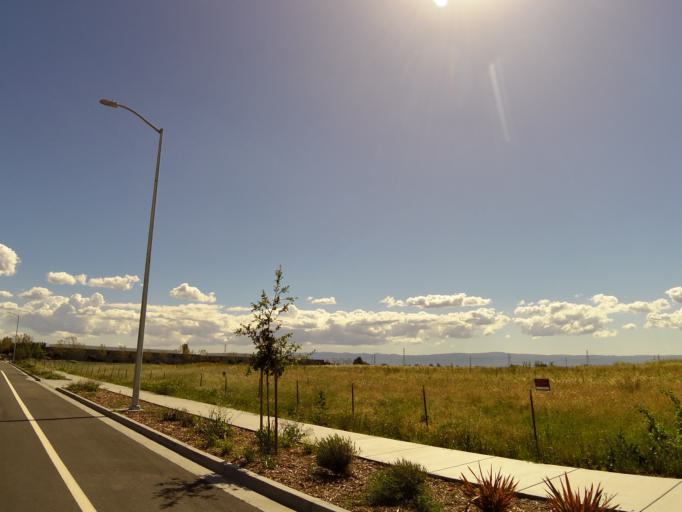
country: US
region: California
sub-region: Santa Clara County
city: Milpitas
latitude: 37.4877
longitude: -121.9470
